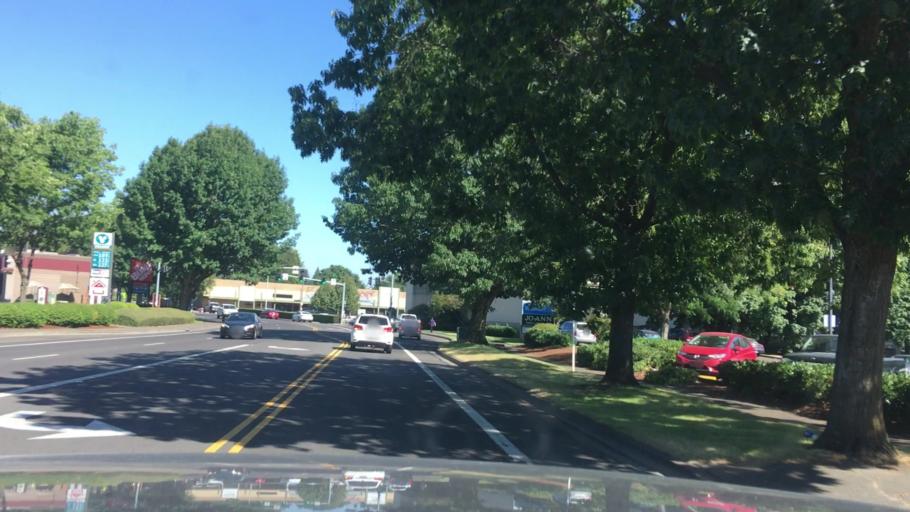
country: US
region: Oregon
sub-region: Lane County
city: Eugene
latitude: 44.0937
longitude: -123.0966
